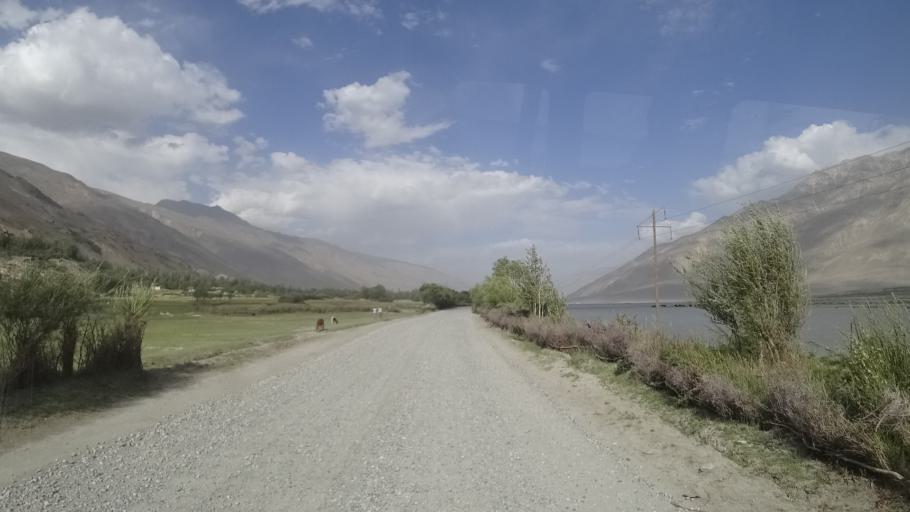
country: AF
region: Badakhshan
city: Khandud
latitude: 36.9775
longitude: 72.3098
